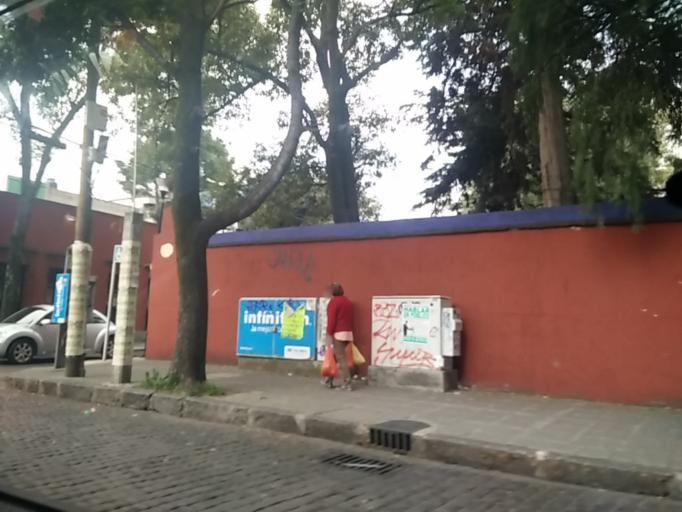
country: MX
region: Mexico City
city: Coyoacan
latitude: 19.3480
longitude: -99.1646
